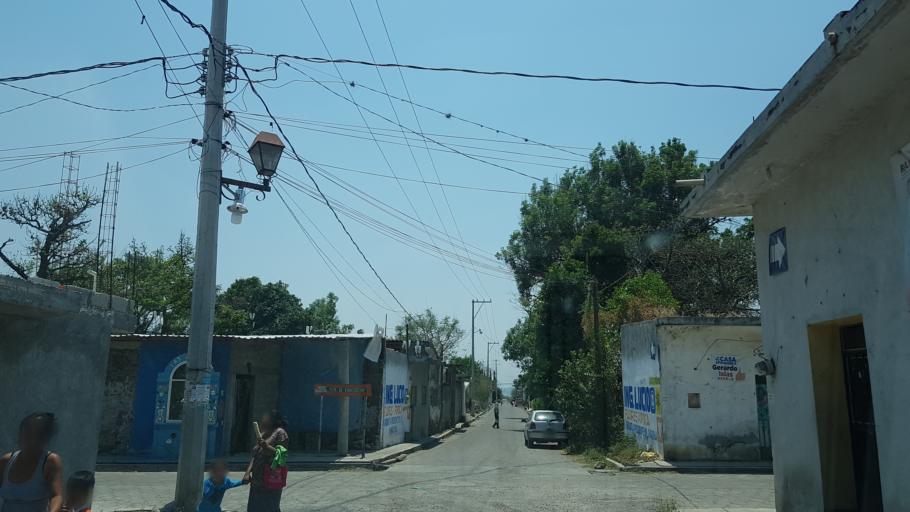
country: MX
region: Puebla
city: Huaquechula
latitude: 18.7730
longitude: -98.5457
